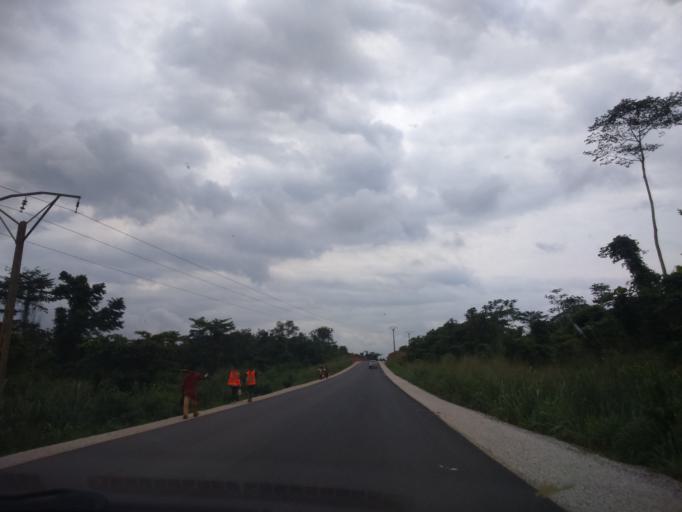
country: CI
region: Lagunes
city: Akoupe
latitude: 6.3294
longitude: -3.8427
